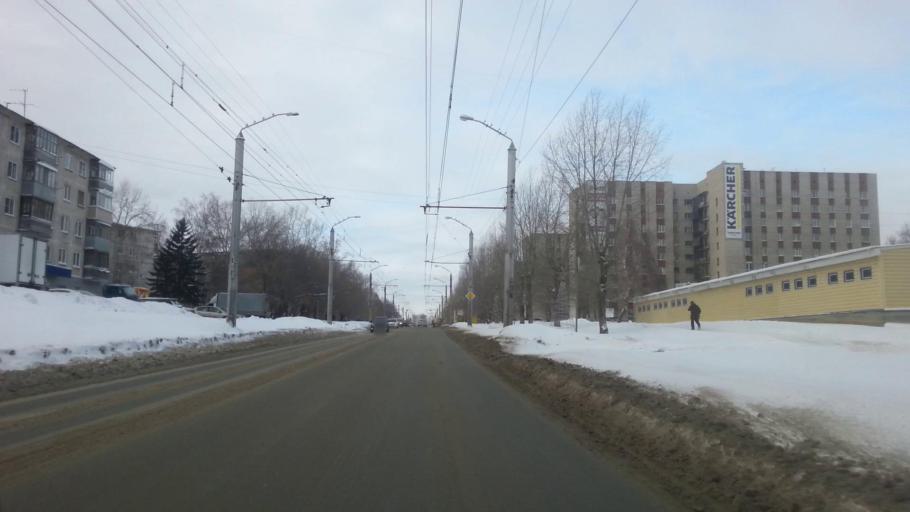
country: RU
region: Altai Krai
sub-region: Gorod Barnaulskiy
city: Barnaul
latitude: 53.3692
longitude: 83.7005
